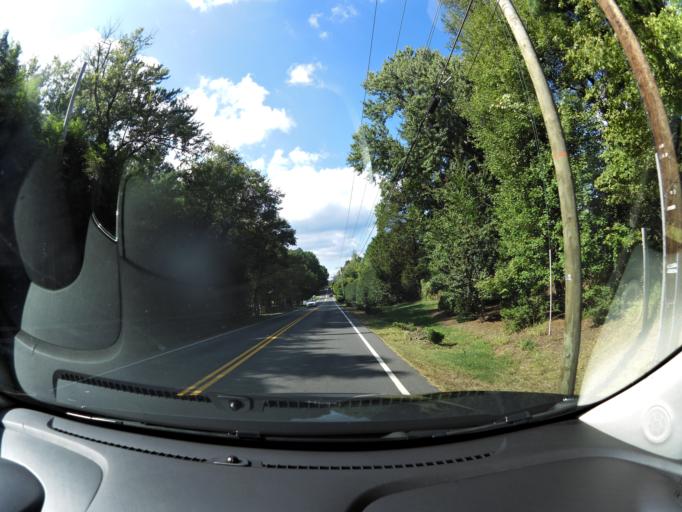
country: US
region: Virginia
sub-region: Fairfax County
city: Great Falls
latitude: 38.9913
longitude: -77.2742
